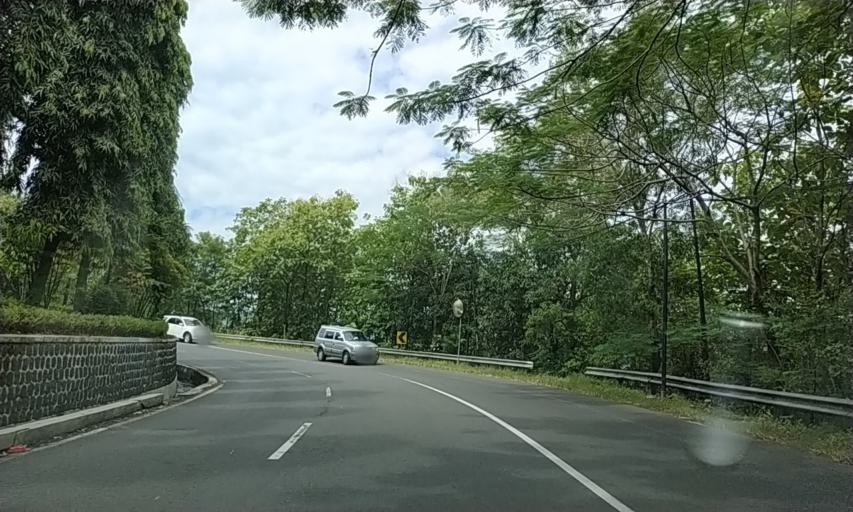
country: ID
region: Central Java
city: Selogiri
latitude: -7.7950
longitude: 110.9018
